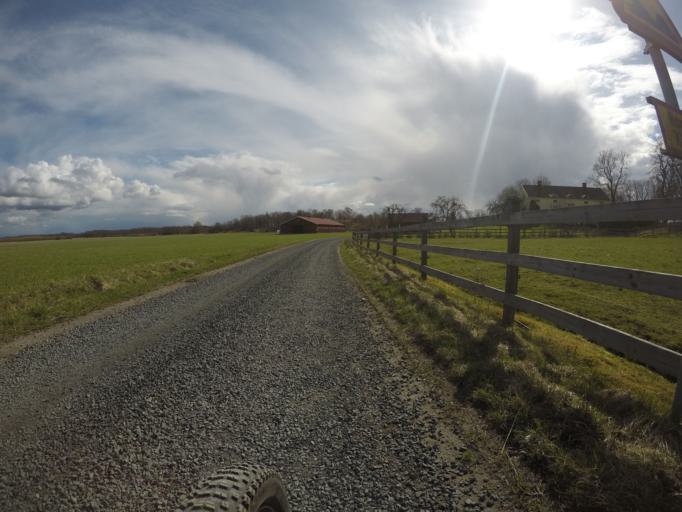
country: SE
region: Vaestmanland
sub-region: Kungsors Kommun
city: Kungsoer
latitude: 59.2819
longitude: 16.1534
